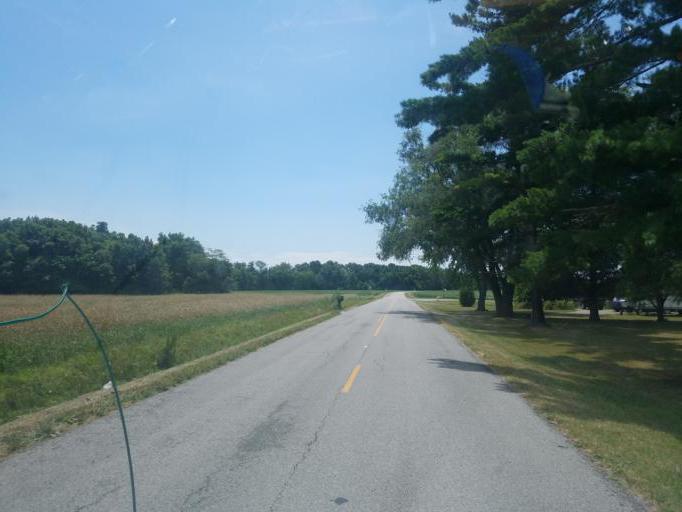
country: US
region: Ohio
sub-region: Paulding County
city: Antwerp
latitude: 41.1923
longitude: -84.7649
